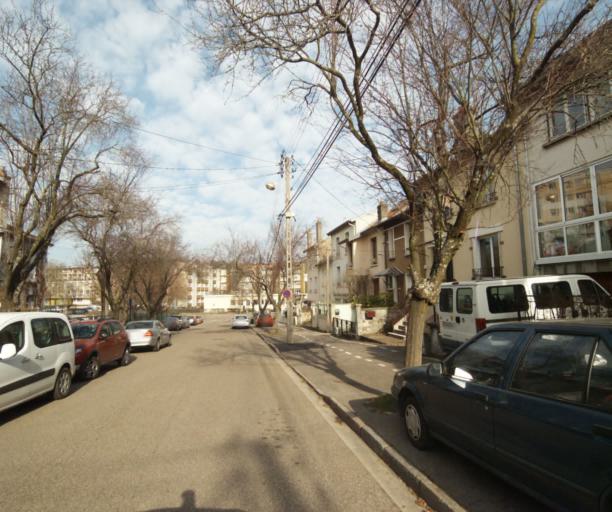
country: FR
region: Lorraine
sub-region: Departement de Meurthe-et-Moselle
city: Laxou
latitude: 48.6800
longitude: 6.1561
